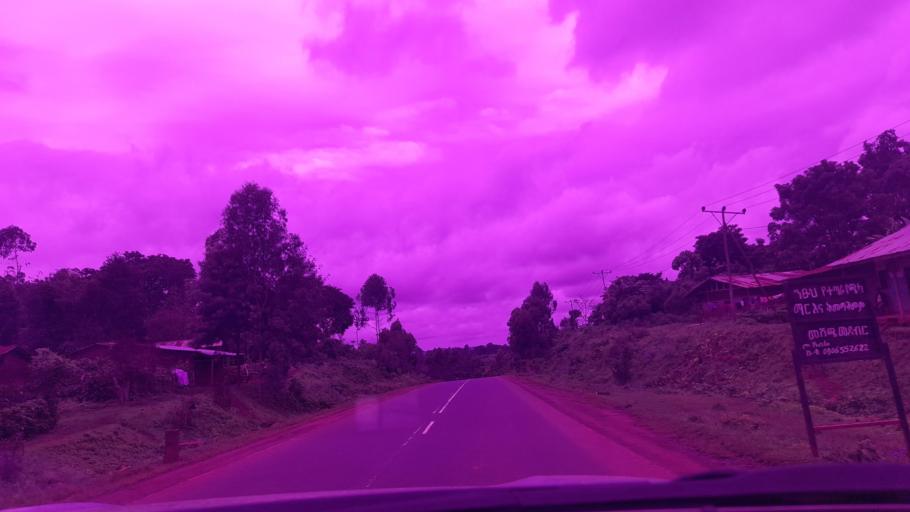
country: ET
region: Southern Nations, Nationalities, and People's Region
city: Bonga
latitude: 7.2938
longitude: 35.9851
